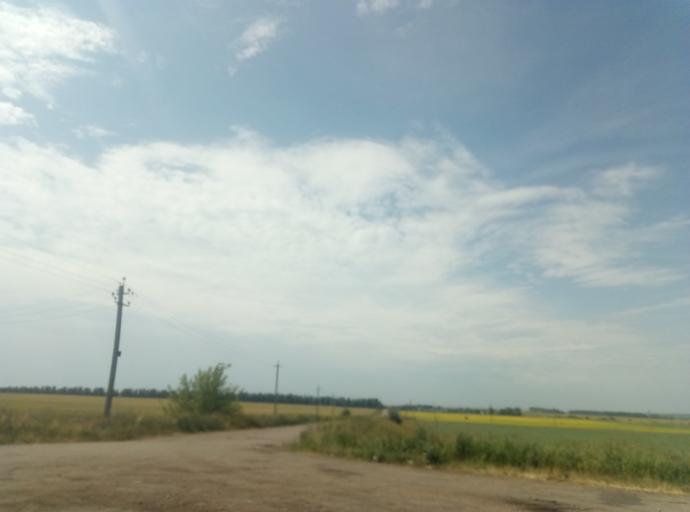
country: RU
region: Tula
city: Dubovka
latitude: 53.8932
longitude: 38.0458
